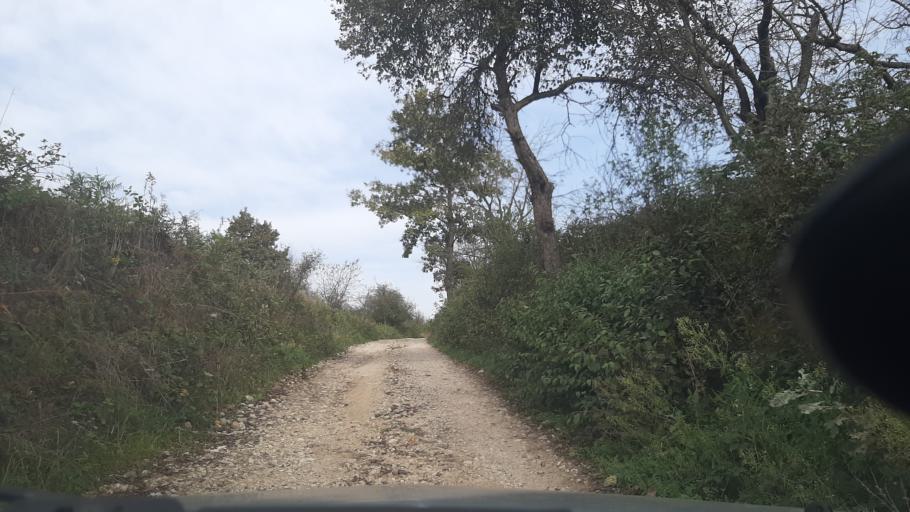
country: BA
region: Republika Srpska
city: Maglajani
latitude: 44.8744
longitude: 17.4718
